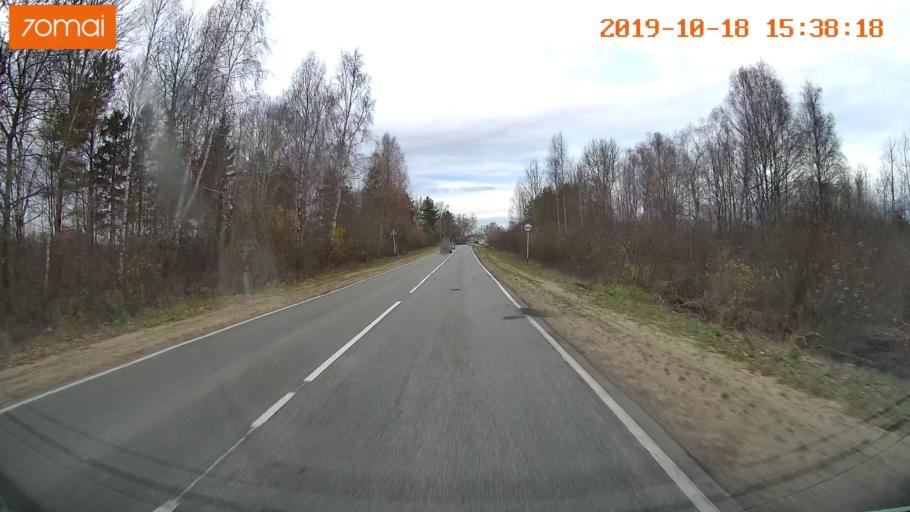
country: RU
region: Vladimir
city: Golovino
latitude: 55.9092
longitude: 40.6081
